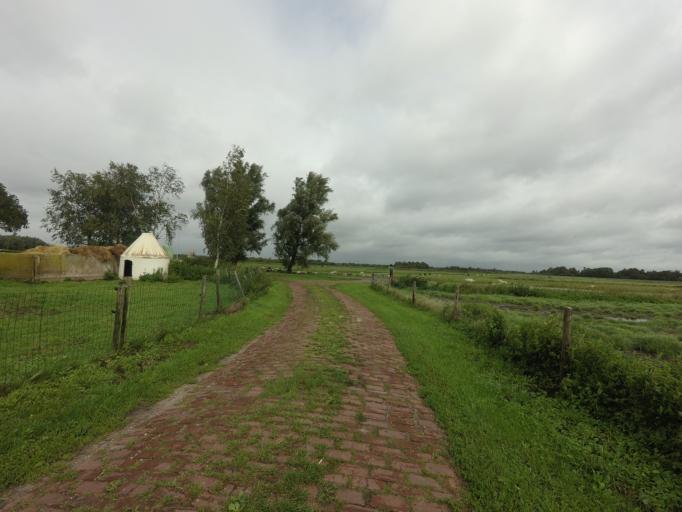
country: NL
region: Overijssel
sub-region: Gemeente Steenwijkerland
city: Blokzijl
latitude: 52.7545
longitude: 5.9683
